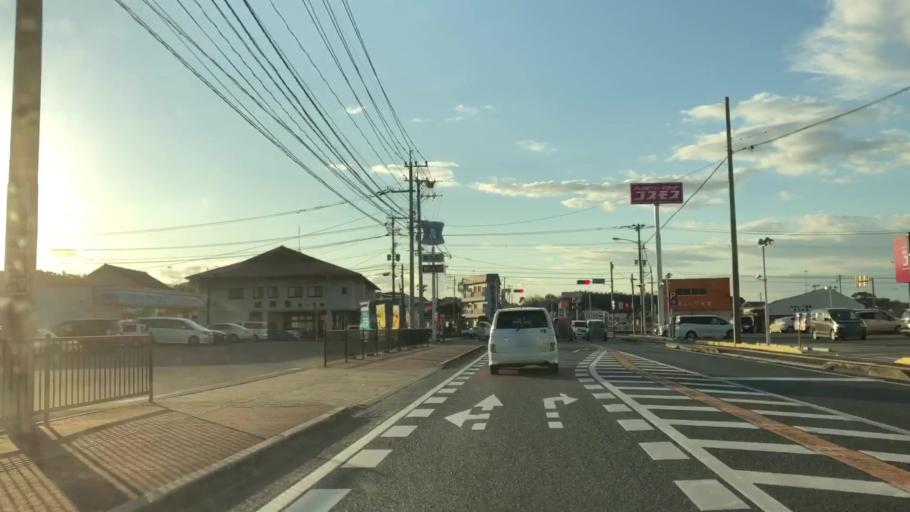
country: JP
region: Oita
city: Bungo-Takada-shi
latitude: 33.5349
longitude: 131.3240
